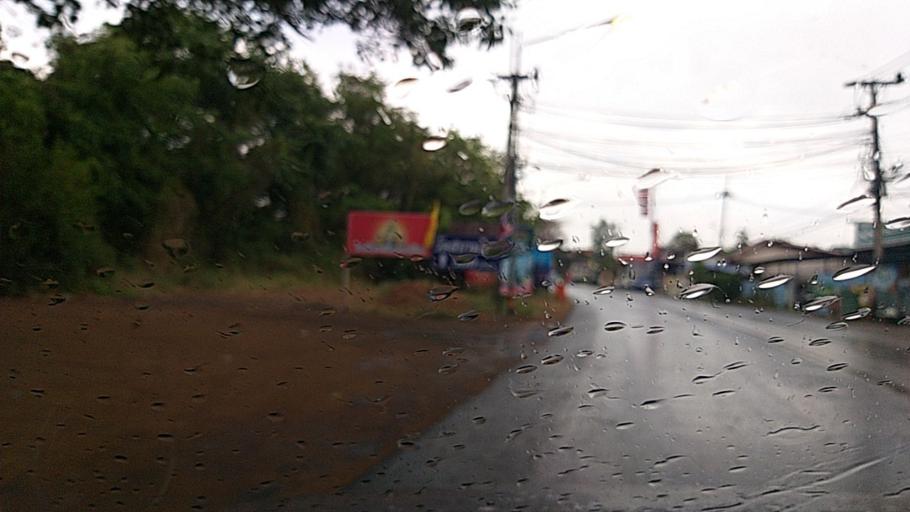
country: TH
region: Phra Nakhon Si Ayutthaya
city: Phra Nakhon Si Ayutthaya
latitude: 14.3414
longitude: 100.5401
